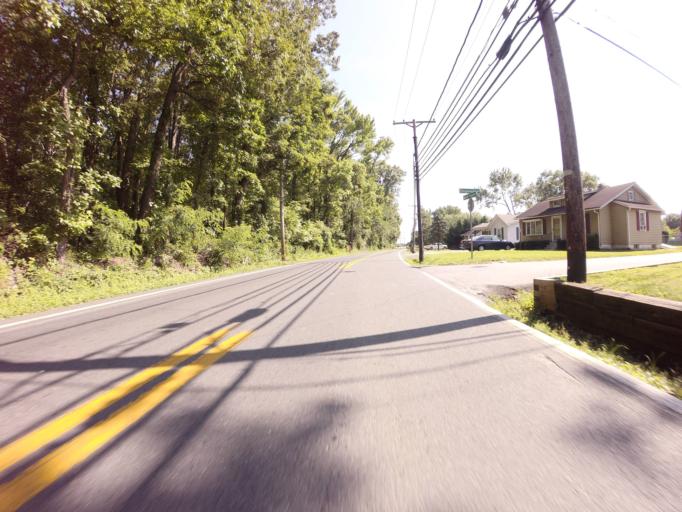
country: US
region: Maryland
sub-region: Baltimore County
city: Edgemere
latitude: 39.2229
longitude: -76.4312
